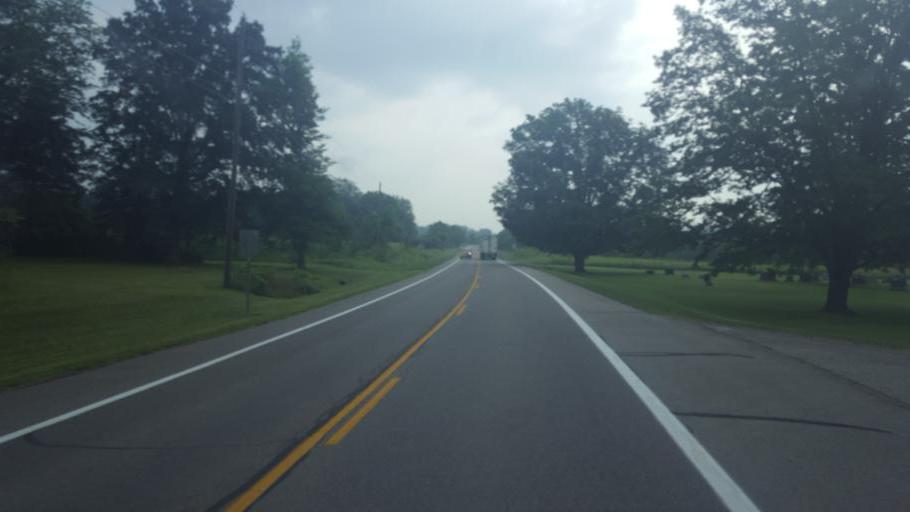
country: US
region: Ohio
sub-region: Morrow County
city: Cardington
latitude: 40.5834
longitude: -82.9937
